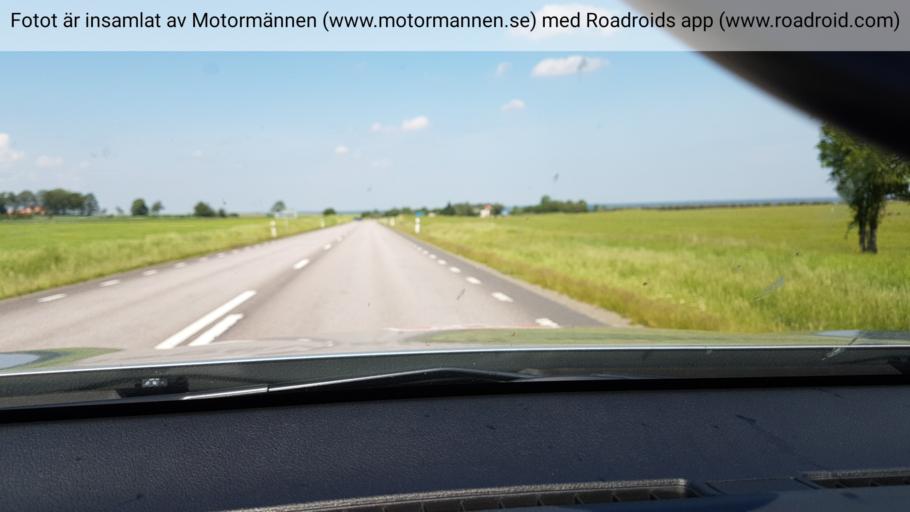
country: SE
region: Vaestra Goetaland
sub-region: Falkopings Kommun
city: Falkoeping
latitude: 58.2287
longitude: 13.5584
